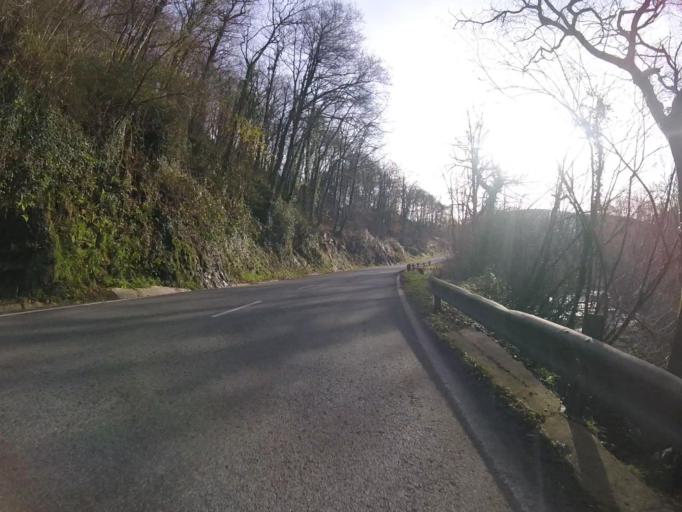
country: ES
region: Navarre
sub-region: Provincia de Navarra
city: Areso
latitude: 43.0953
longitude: -1.9413
